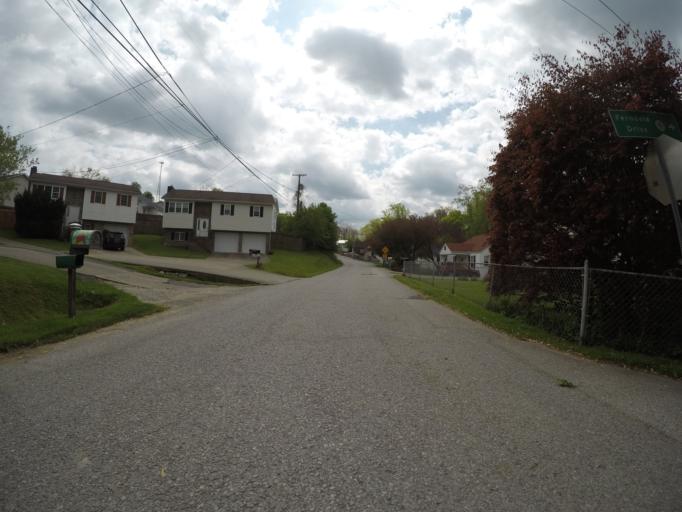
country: US
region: West Virginia
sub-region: Kanawha County
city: Charleston
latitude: 38.3917
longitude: -81.6014
